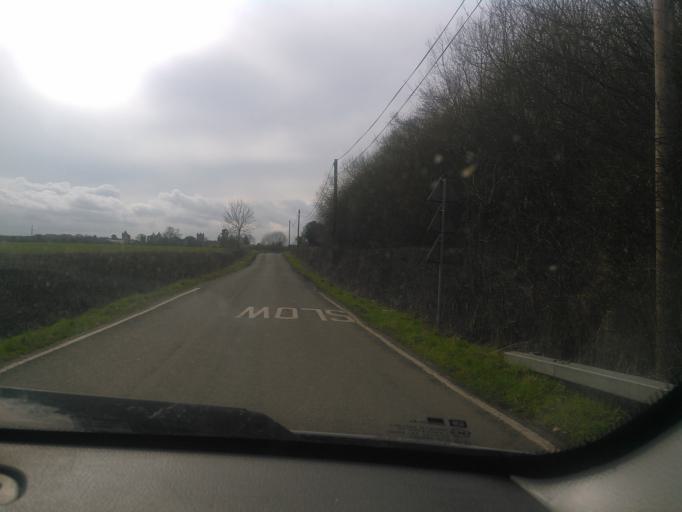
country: GB
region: England
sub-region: Shropshire
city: Shawbury
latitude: 52.8111
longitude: -2.6475
